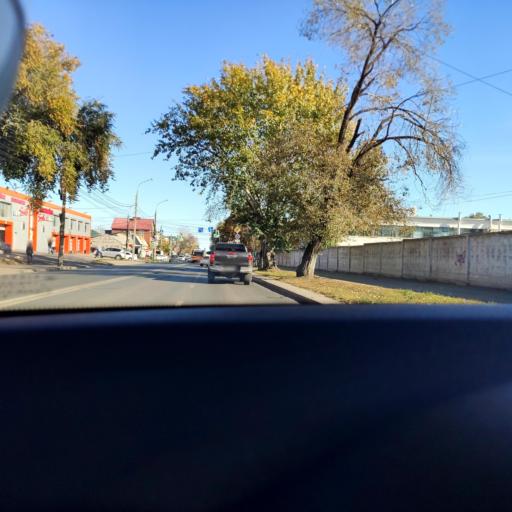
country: RU
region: Samara
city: Samara
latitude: 53.1969
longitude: 50.1886
